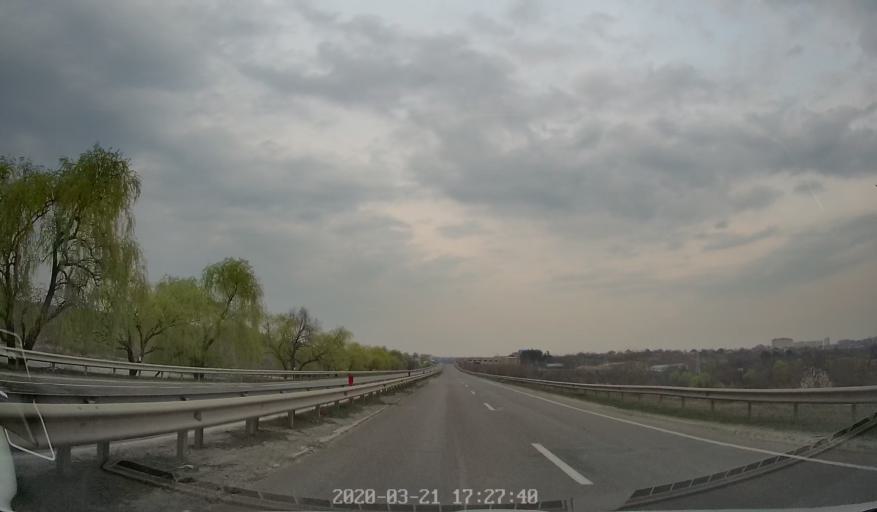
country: MD
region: Laloveni
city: Ialoveni
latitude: 46.9548
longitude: 28.7434
